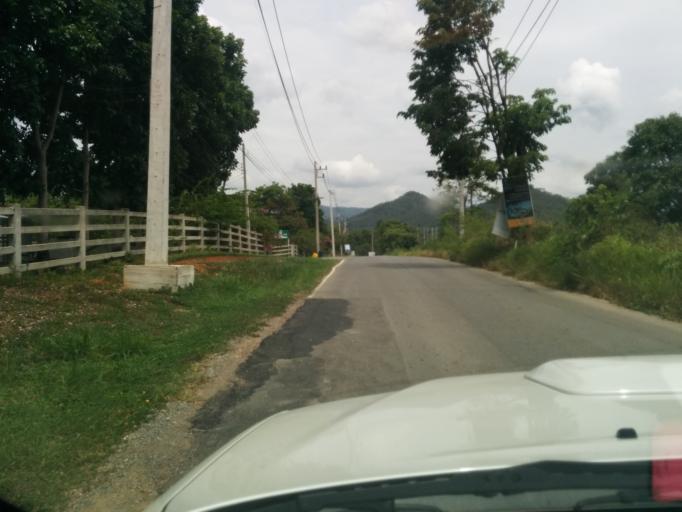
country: TH
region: Sara Buri
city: Muak Lek
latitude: 14.5741
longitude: 101.2390
